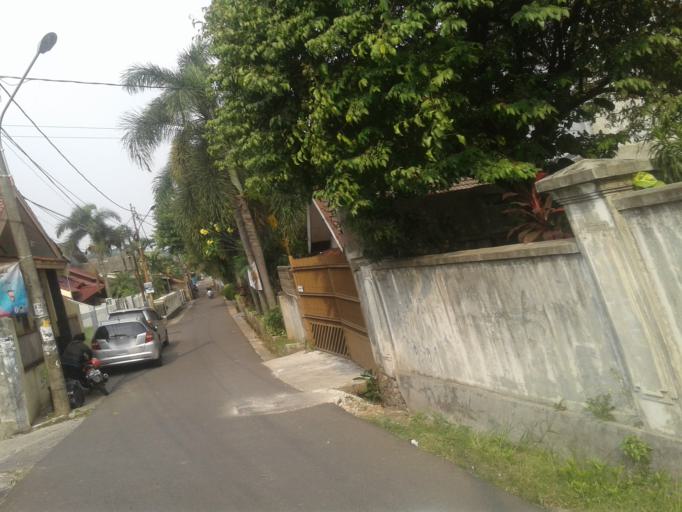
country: ID
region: West Java
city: Depok
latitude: -6.3704
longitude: 106.8357
